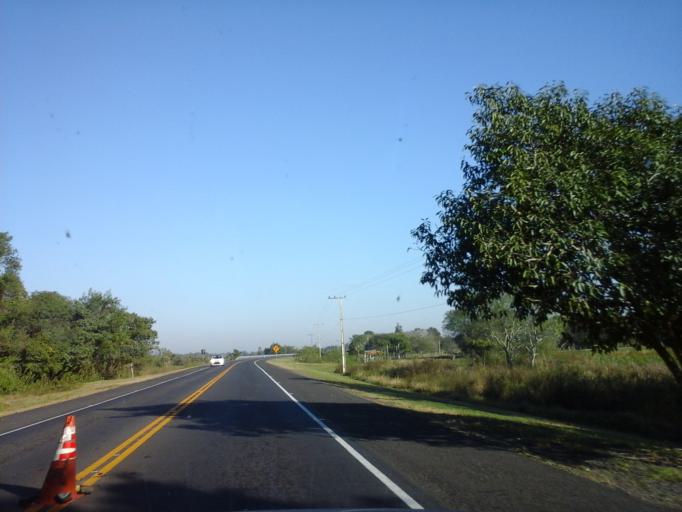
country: PY
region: Neembucu
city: Pilar
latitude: -26.8654
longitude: -58.1471
